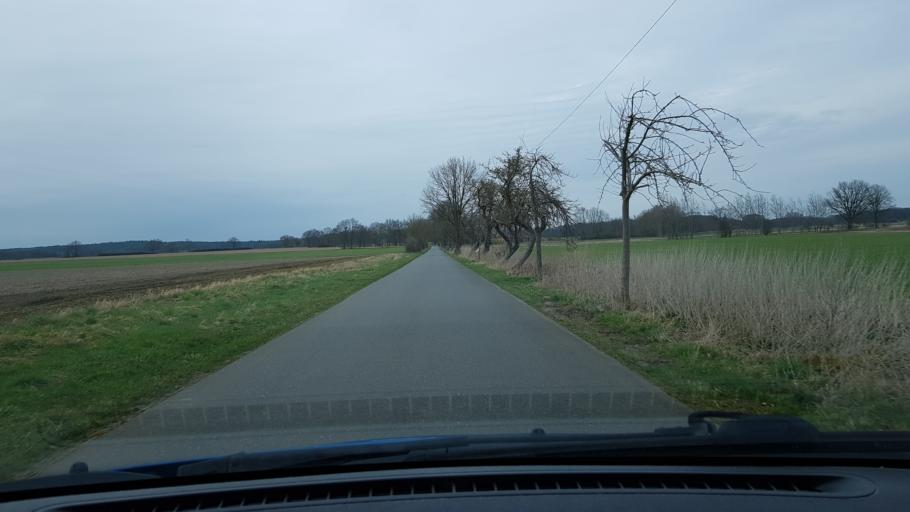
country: DE
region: Lower Saxony
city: Oetzen
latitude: 53.0015
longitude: 10.6520
